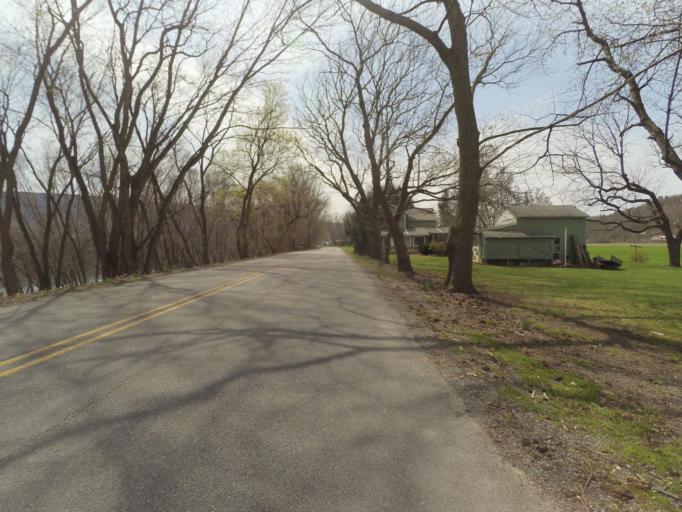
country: US
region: Pennsylvania
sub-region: Clinton County
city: Dunnstown
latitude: 41.1597
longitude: -77.3764
